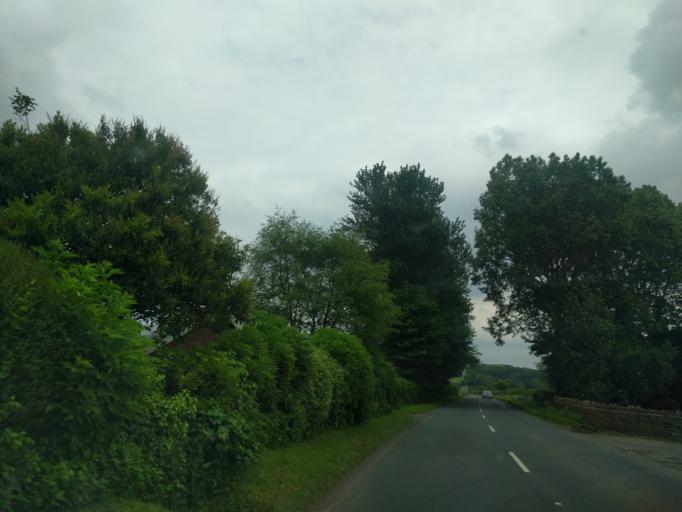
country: GB
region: England
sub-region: Somerset
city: Ilchester
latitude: 51.0738
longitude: -2.6718
